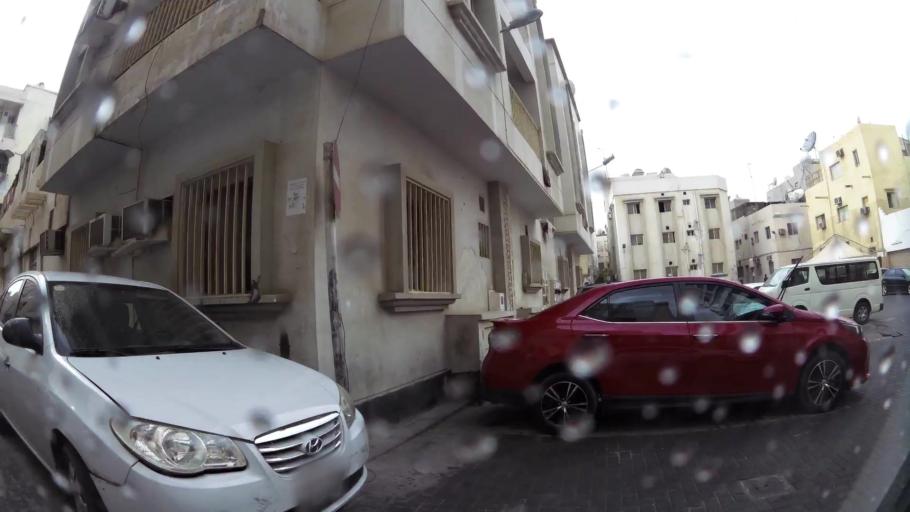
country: BH
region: Manama
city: Manama
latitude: 26.2314
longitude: 50.5949
